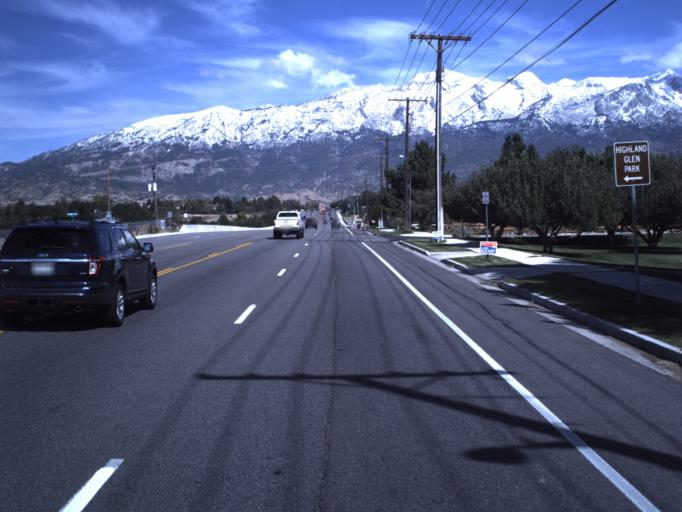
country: US
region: Utah
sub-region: Utah County
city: Cedar Hills
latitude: 40.4220
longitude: -111.7734
